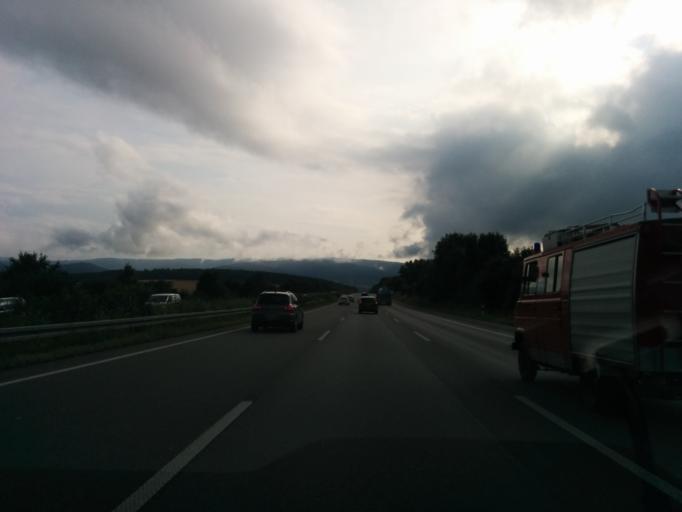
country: DE
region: Lower Saxony
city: Juhnde
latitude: 51.4072
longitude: 9.8182
